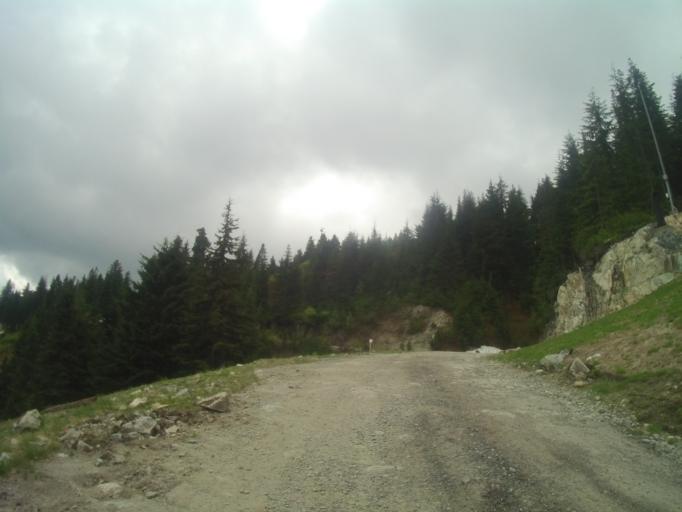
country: CA
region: British Columbia
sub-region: Fraser Valley Regional District
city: North Vancouver
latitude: 49.3815
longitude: -123.0727
